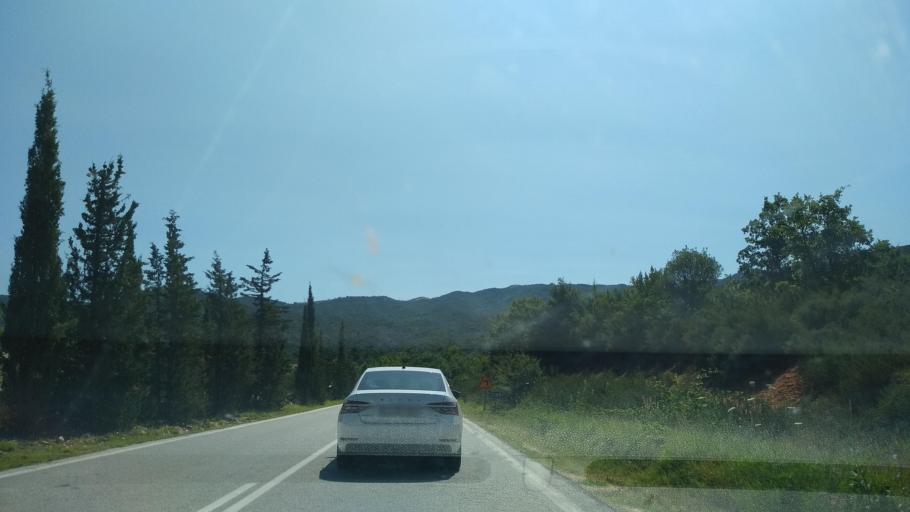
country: GR
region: Central Macedonia
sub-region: Nomos Chalkidikis
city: Arnaia
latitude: 40.5005
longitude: 23.5215
